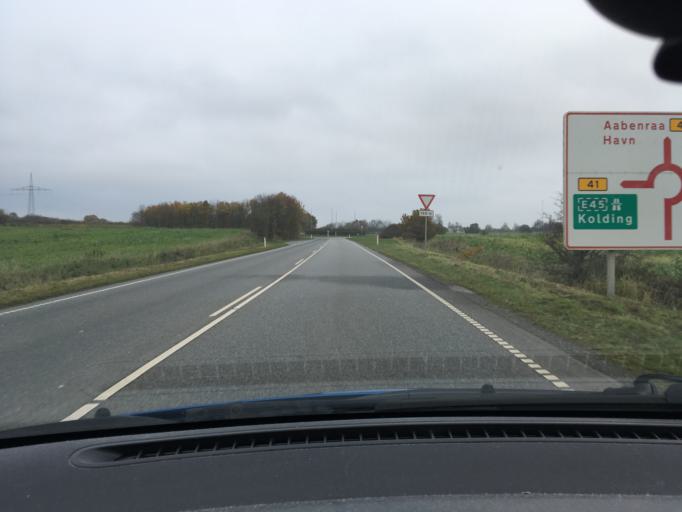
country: DK
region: South Denmark
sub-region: Aabenraa Kommune
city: Aabenraa
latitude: 55.0007
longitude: 9.4170
